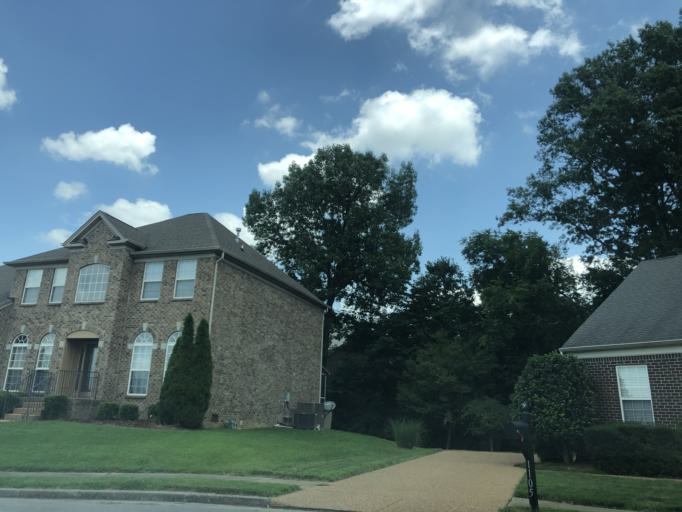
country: US
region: Tennessee
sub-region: Williamson County
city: Brentwood Estates
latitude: 36.0103
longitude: -86.7291
